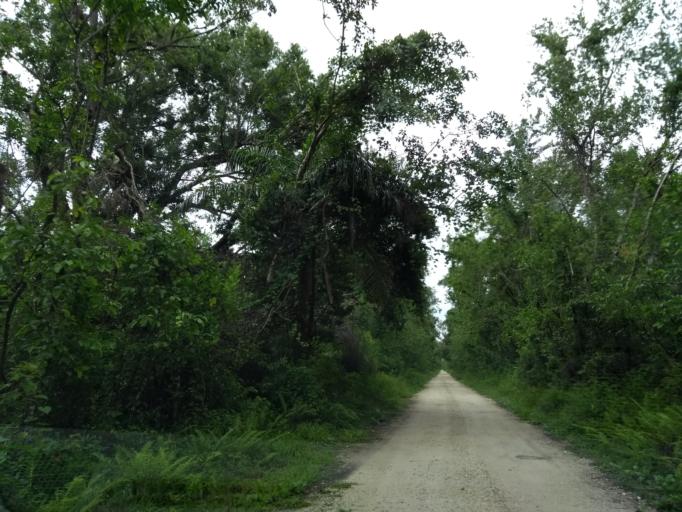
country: US
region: Florida
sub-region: Collier County
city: Lely Resort
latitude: 26.0033
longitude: -81.4112
